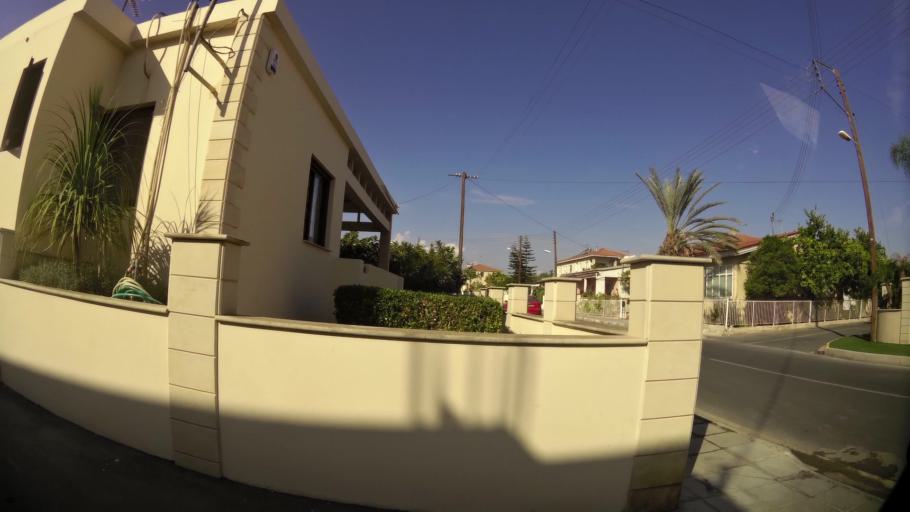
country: CY
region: Larnaka
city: Aradippou
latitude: 34.9523
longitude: 33.5866
